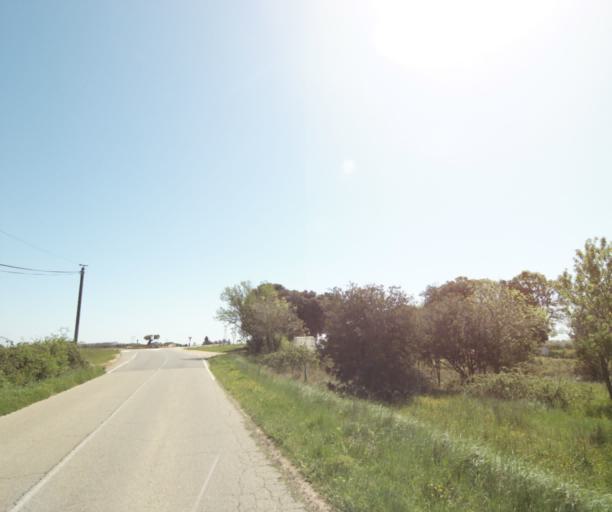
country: FR
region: Languedoc-Roussillon
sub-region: Departement de l'Herault
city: Baillargues
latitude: 43.6652
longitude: 4.0003
